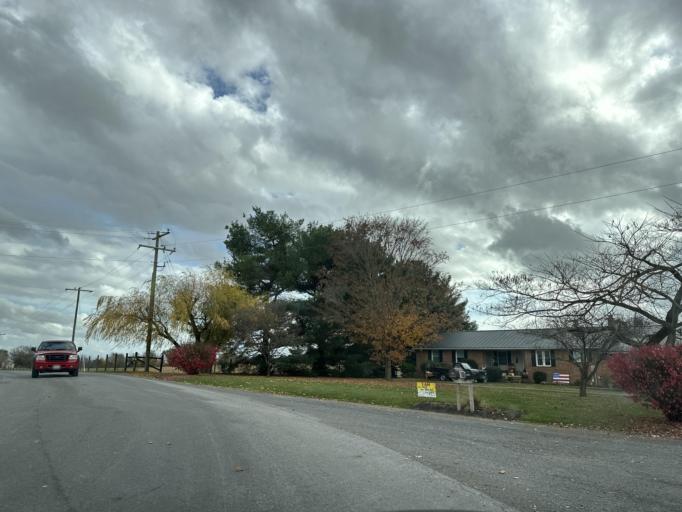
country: US
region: Virginia
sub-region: Rockingham County
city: Dayton
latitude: 38.4141
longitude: -78.9677
